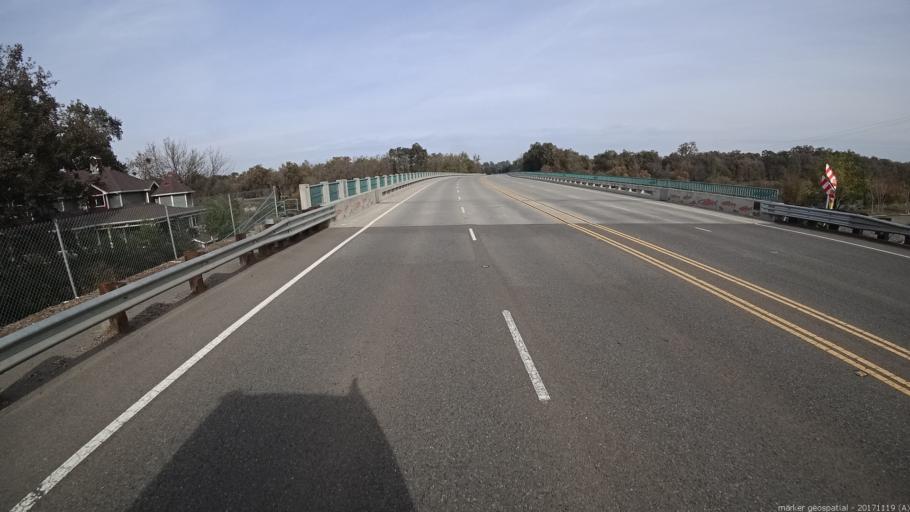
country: US
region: California
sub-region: Shasta County
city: Anderson
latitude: 40.4709
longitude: -122.2952
